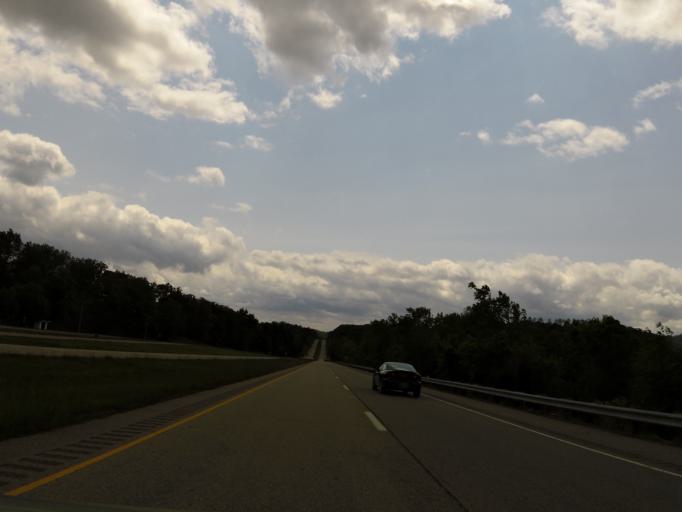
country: US
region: Ohio
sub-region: Meigs County
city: Pomeroy
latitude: 39.1197
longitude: -82.0170
